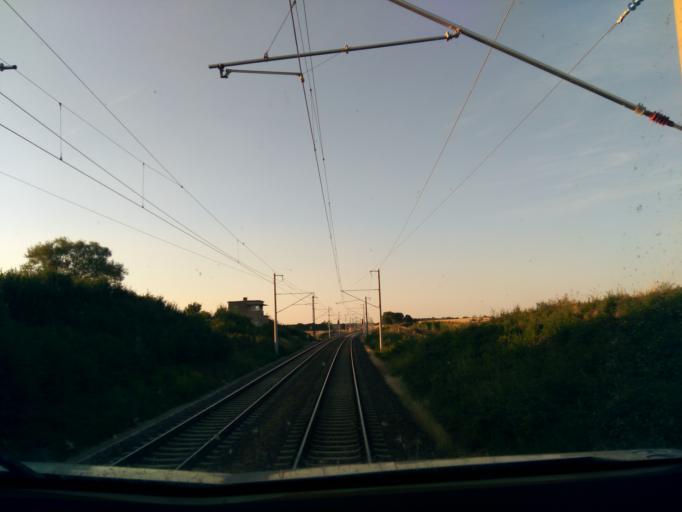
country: DE
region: Mecklenburg-Vorpommern
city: Seehof
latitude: 53.6827
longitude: 11.4085
